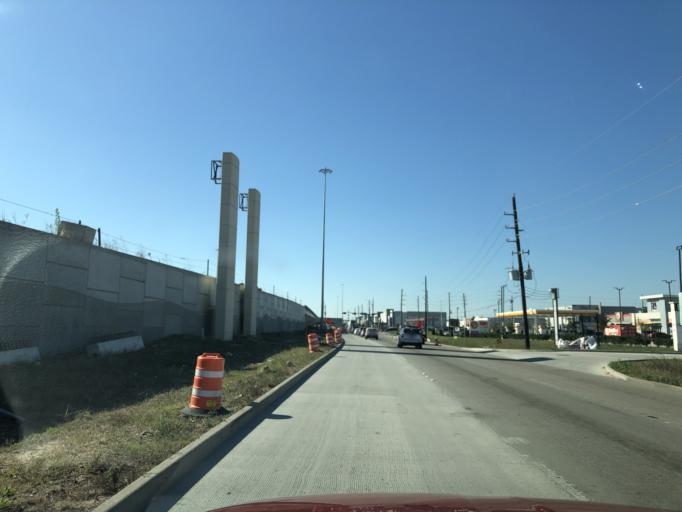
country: US
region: Texas
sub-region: Brazoria County
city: Brookside Village
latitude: 29.5984
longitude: -95.3660
